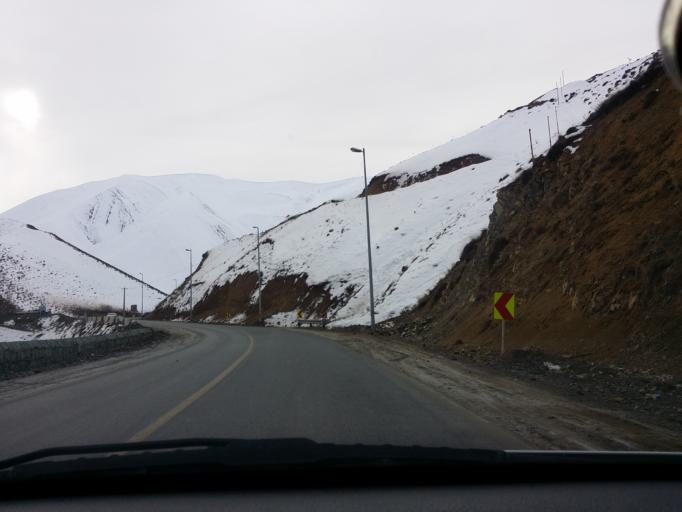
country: IR
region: Tehran
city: Tajrish
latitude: 36.1644
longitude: 51.3155
